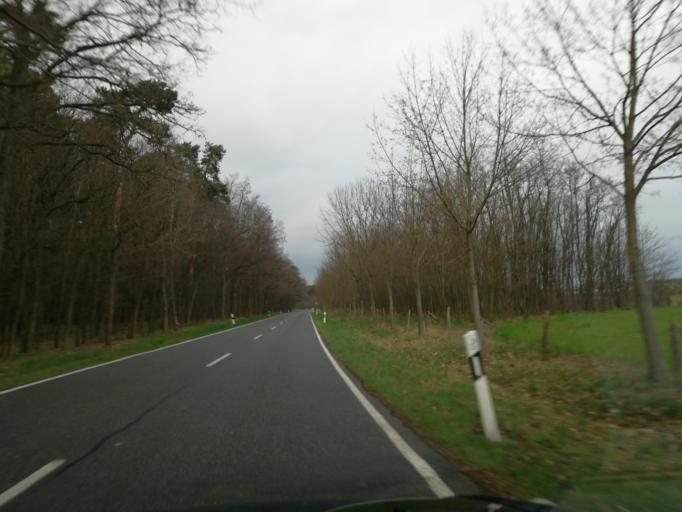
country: DE
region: Brandenburg
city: Vetschau
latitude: 51.7204
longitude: 14.0929
